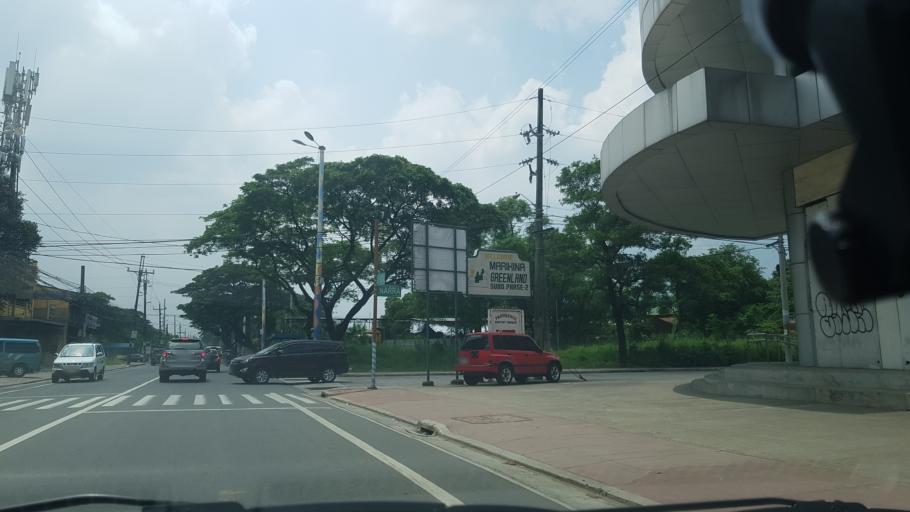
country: PH
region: Calabarzon
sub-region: Province of Rizal
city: San Mateo
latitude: 14.6683
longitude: 121.1079
